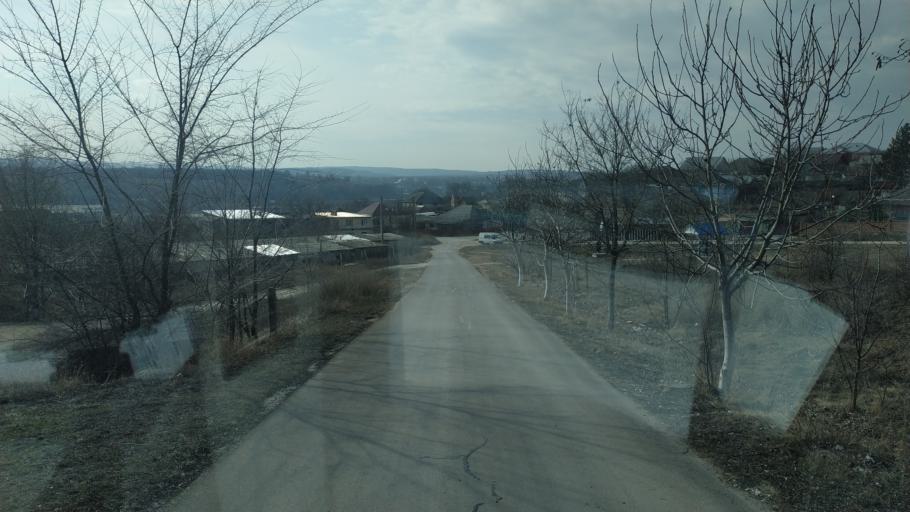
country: MD
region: Chisinau
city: Singera
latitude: 46.9279
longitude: 29.0667
